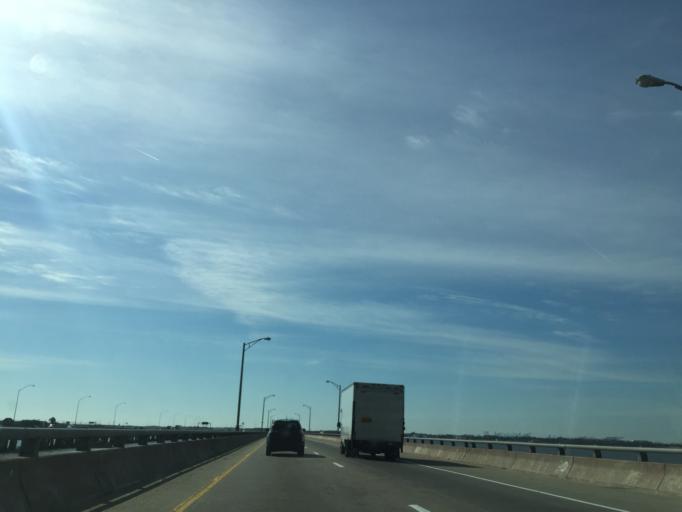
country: US
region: Virginia
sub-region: City of Hampton
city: East Hampton
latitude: 36.9764
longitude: -76.3009
